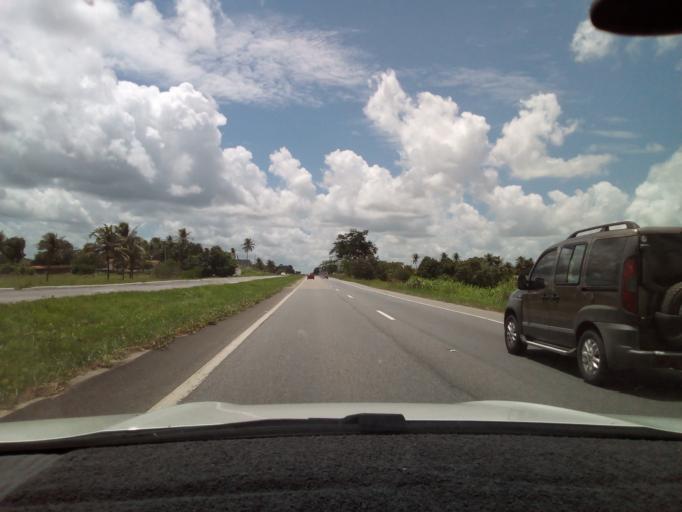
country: BR
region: Paraiba
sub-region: Pilar
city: Pilar
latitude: -7.1832
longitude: -35.3029
